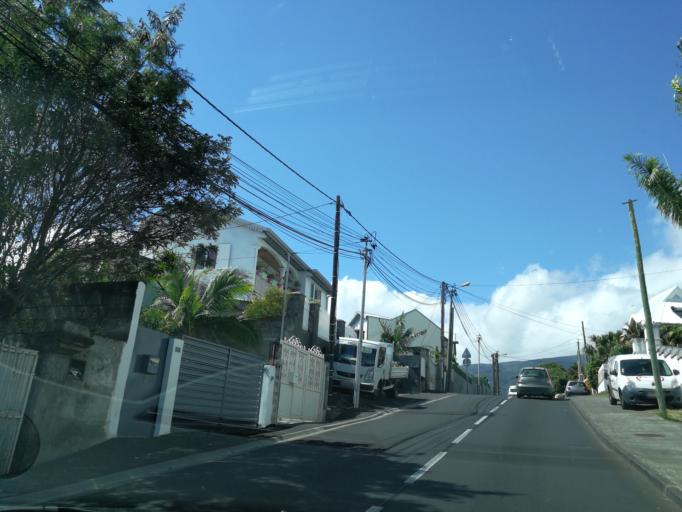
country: RE
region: Reunion
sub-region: Reunion
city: Saint-Denis
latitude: -20.9109
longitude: 55.4817
